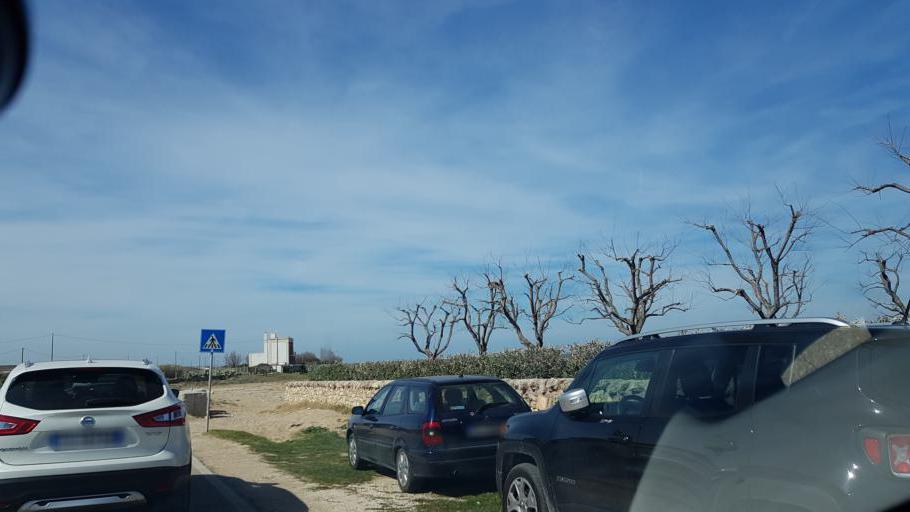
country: IT
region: Apulia
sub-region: Provincia di Brindisi
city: Pezze di Greco
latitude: 40.8538
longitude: 17.4440
